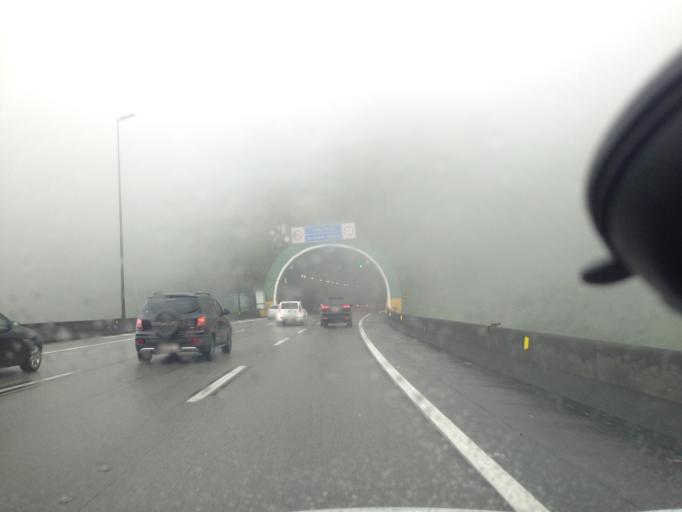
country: BR
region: Sao Paulo
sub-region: Cubatao
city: Cubatao
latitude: -23.8970
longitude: -46.5078
